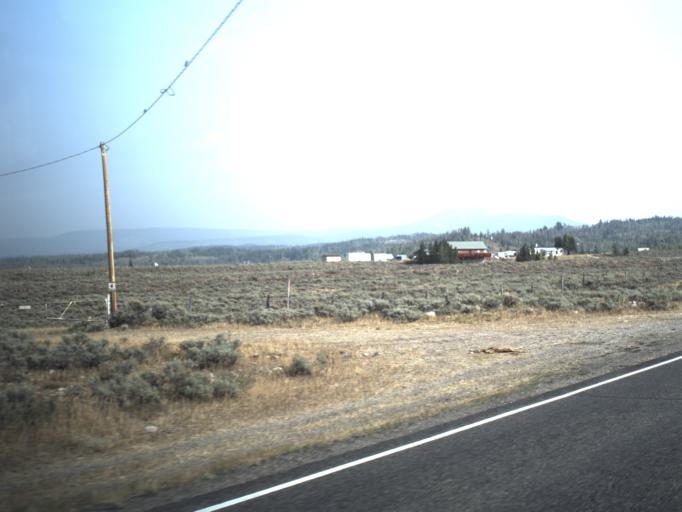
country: US
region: Wyoming
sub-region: Uinta County
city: Evanston
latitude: 40.9447
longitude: -110.8388
